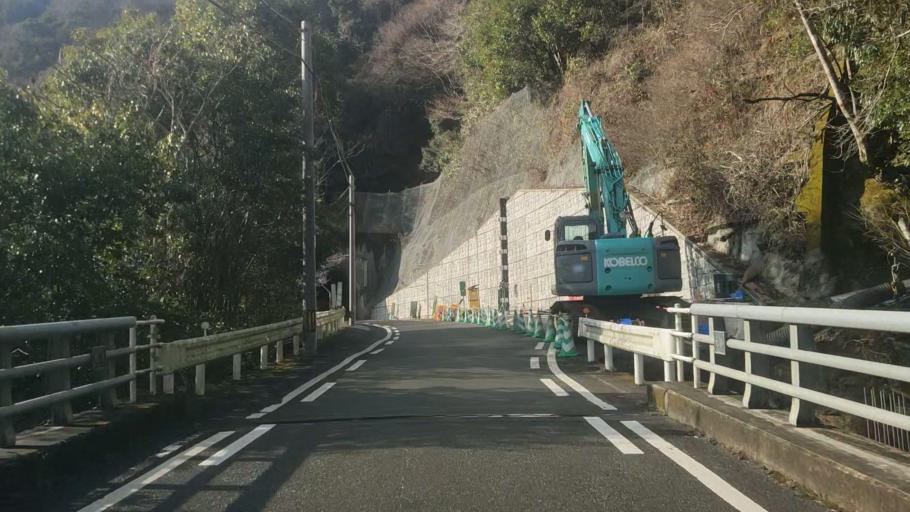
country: JP
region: Kumamoto
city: Hitoyoshi
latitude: 32.4176
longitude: 130.8457
